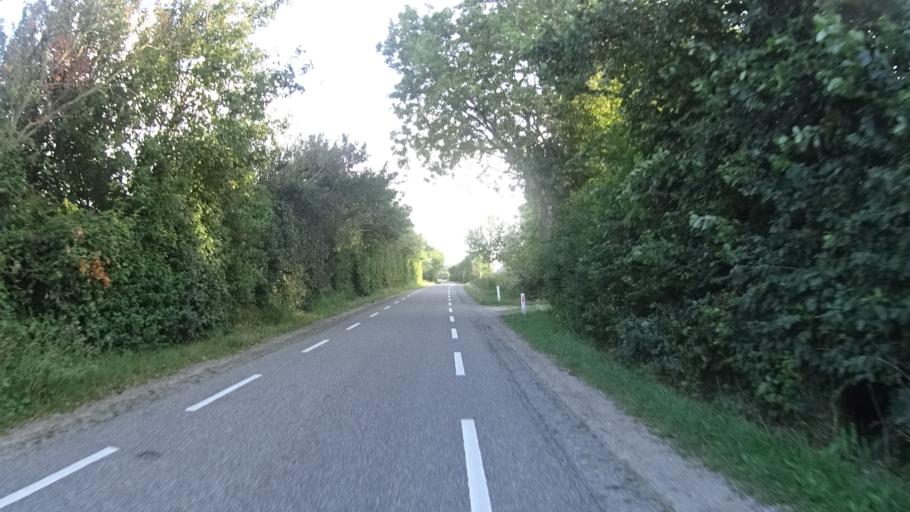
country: NL
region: Zeeland
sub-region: Gemeente Middelburg
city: Middelburg
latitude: 51.5233
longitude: 3.6299
